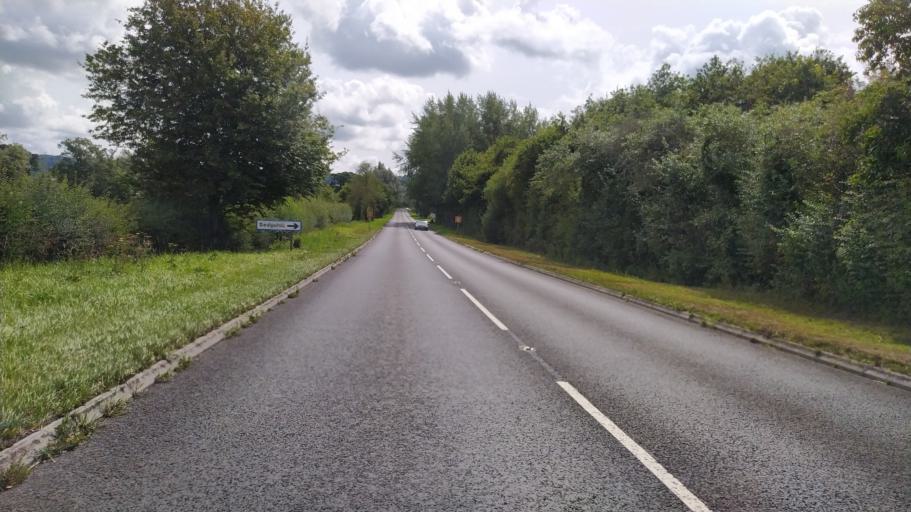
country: GB
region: England
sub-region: Dorset
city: Shaftesbury
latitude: 51.0505
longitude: -2.1835
